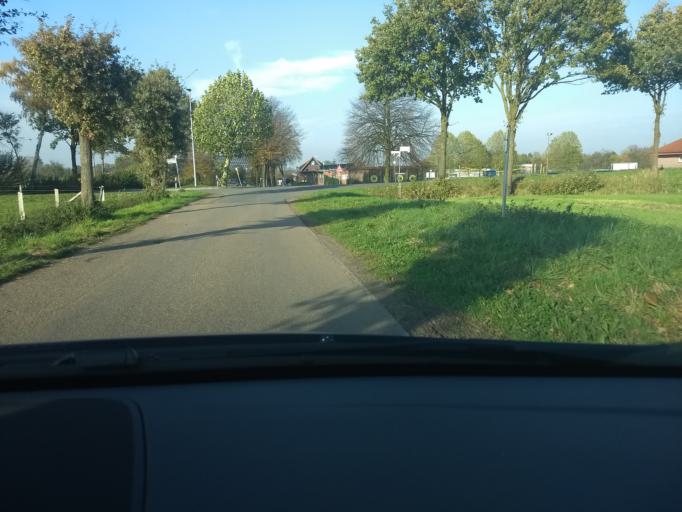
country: DE
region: North Rhine-Westphalia
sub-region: Regierungsbezirk Munster
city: Sudlohn
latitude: 51.9094
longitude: 6.8439
